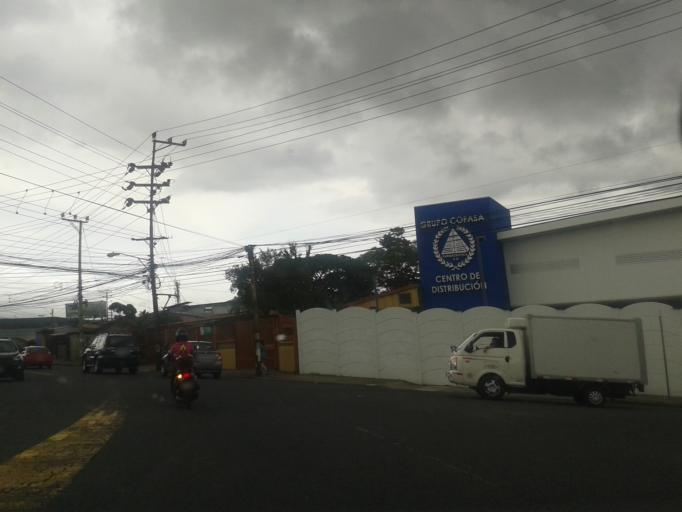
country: CR
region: San Jose
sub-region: Canton de Goicoechea
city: Guadalupe
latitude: 9.9470
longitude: -84.0620
